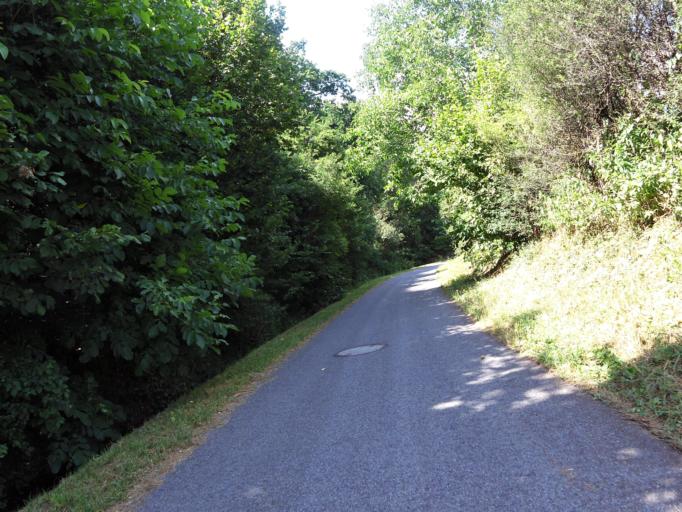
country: DE
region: Bavaria
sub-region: Regierungsbezirk Unterfranken
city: Gerbrunn
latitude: 49.7820
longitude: 9.9951
